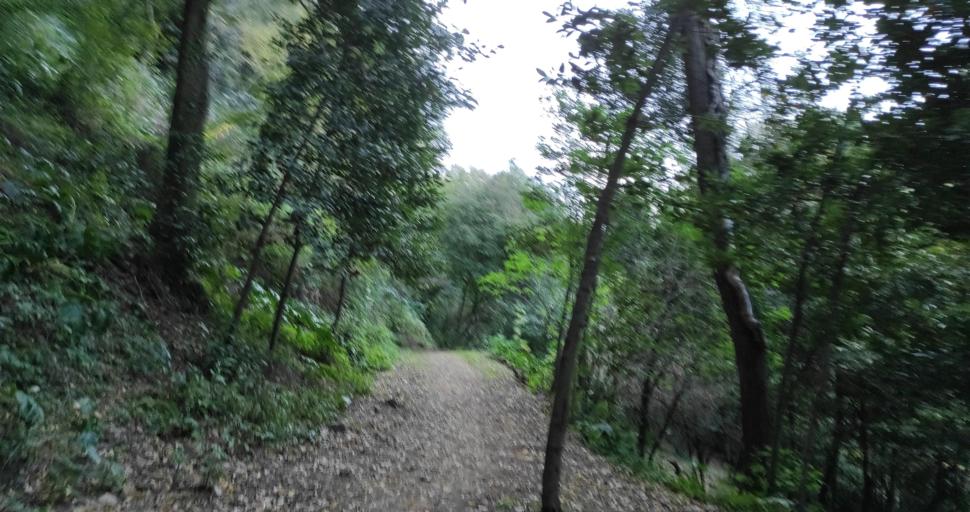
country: ES
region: Catalonia
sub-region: Provincia de Girona
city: Girona
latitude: 41.9878
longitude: 2.8281
